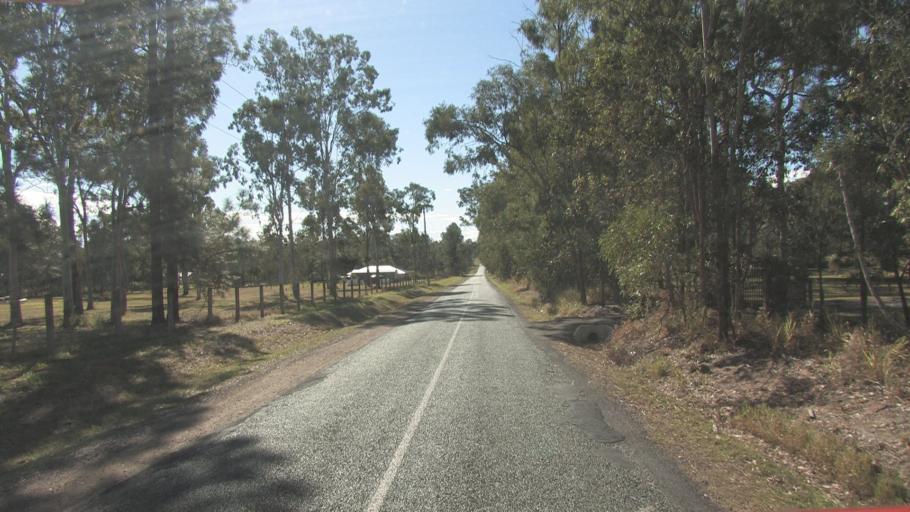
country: AU
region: Queensland
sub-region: Logan
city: Chambers Flat
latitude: -27.8033
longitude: 153.0712
